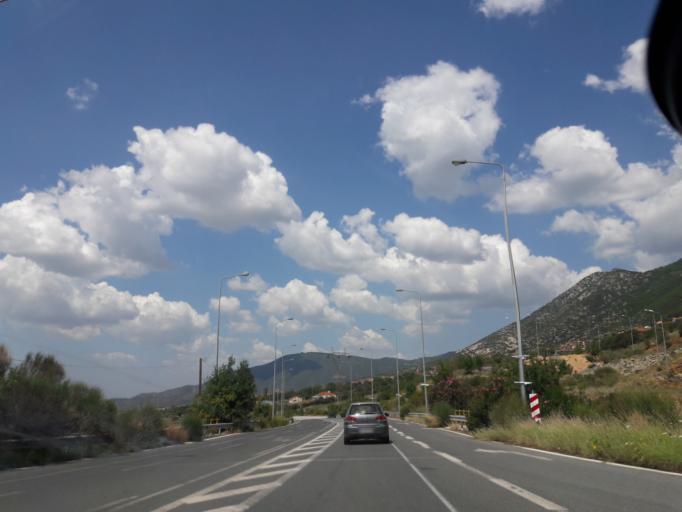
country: GR
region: Central Macedonia
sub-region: Nomos Chalkidikis
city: Galatista
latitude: 40.4590
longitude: 23.2885
